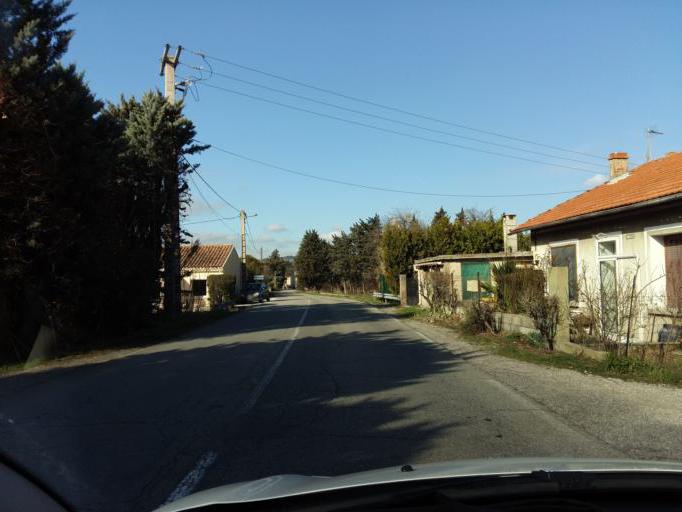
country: FR
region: Provence-Alpes-Cote d'Azur
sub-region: Departement du Vaucluse
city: Cavaillon
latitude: 43.8200
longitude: 5.0520
